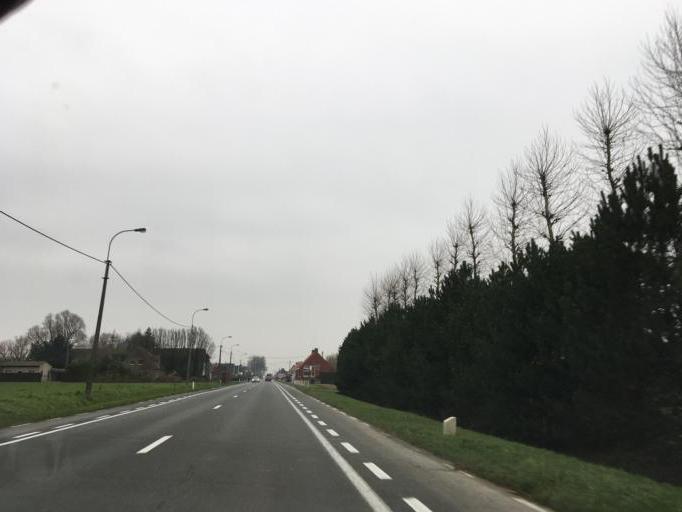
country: BE
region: Flanders
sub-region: Provincie West-Vlaanderen
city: Ingelmunster
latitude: 50.9575
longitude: 3.2454
